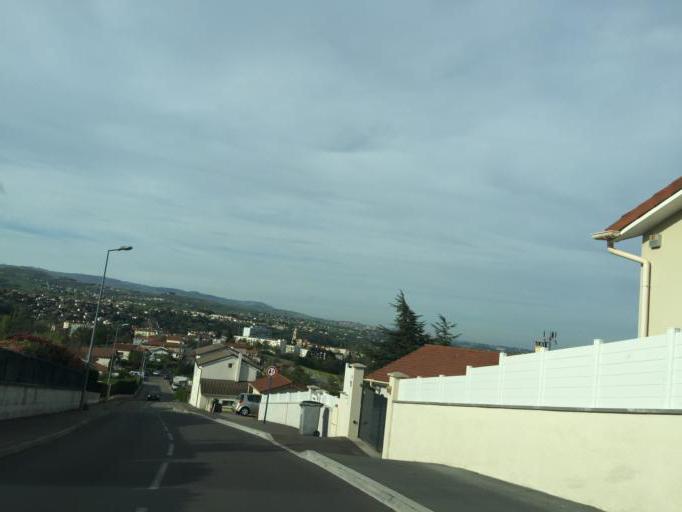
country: FR
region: Rhone-Alpes
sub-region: Departement de la Loire
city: Saint-Chamond
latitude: 45.4761
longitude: 4.5394
